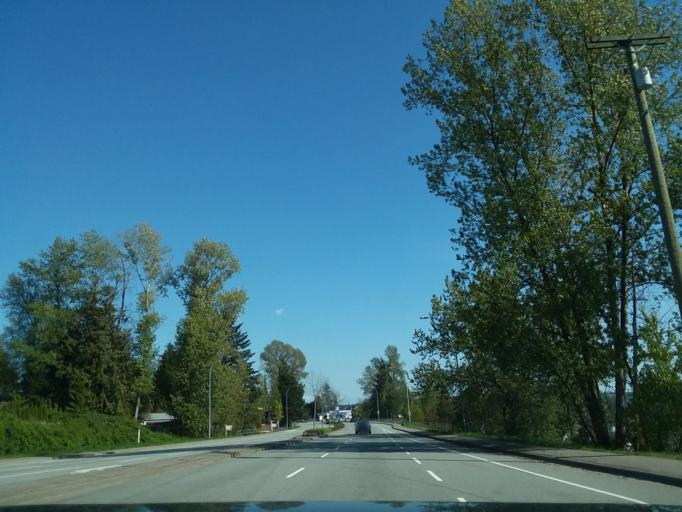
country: CA
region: British Columbia
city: New Westminster
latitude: 49.2394
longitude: -122.8811
